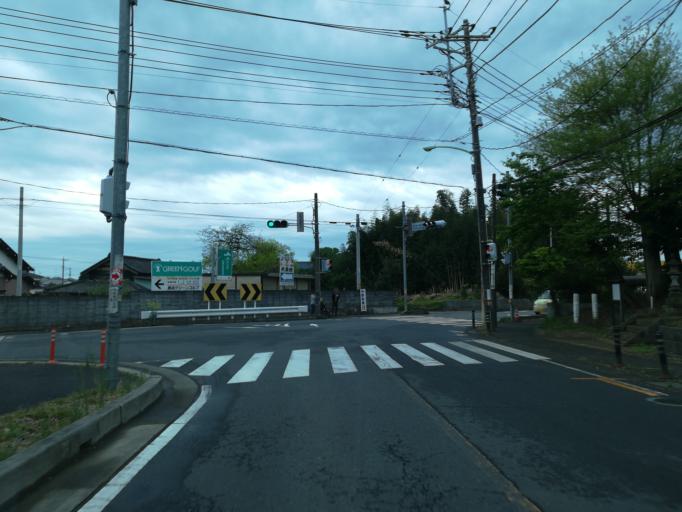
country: JP
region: Saitama
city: Hasuda
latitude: 35.9830
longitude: 139.6702
